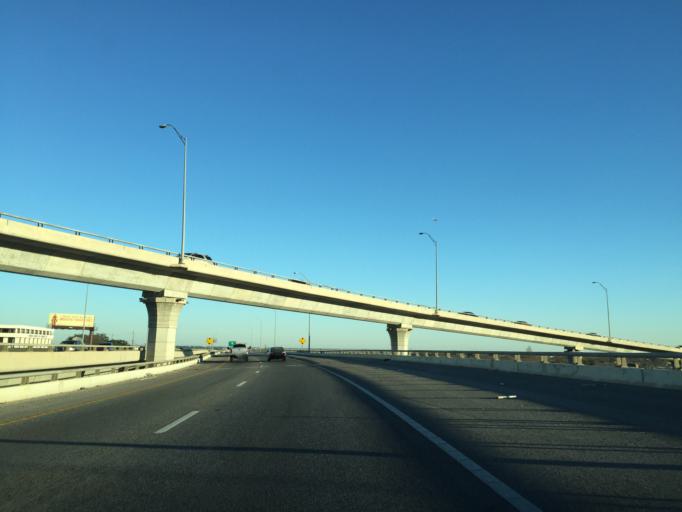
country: US
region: Texas
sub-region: Travis County
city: Austin
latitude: 30.3397
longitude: -97.7011
